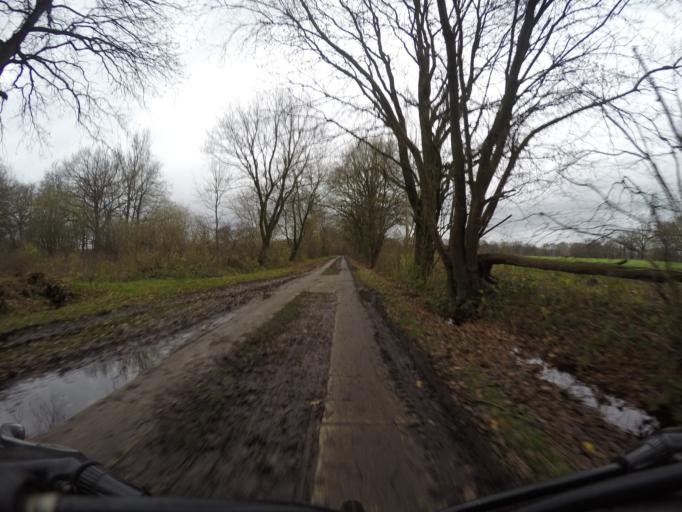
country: DE
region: Schleswig-Holstein
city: Hemdingen
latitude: 53.7247
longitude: 9.8338
